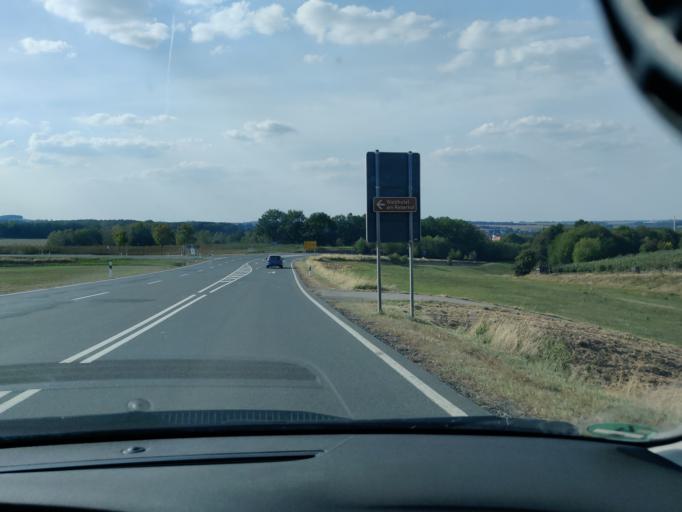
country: DE
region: Saxony
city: Seelitz
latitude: 51.0382
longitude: 12.8179
